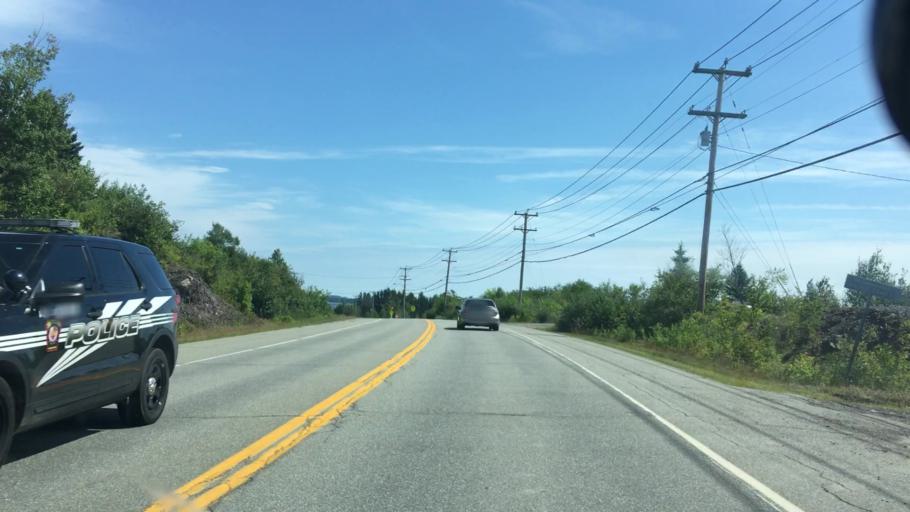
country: US
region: Maine
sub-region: Washington County
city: Eastport
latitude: 44.9568
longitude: -67.0468
